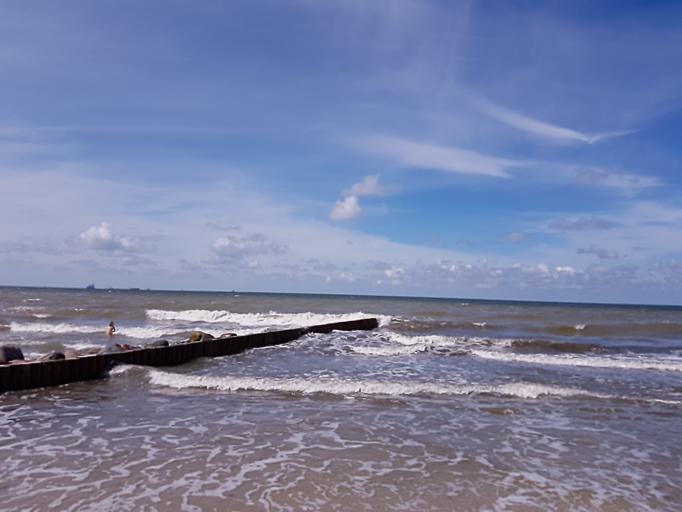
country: RU
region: Kaliningrad
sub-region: Zelenogradskiy Rayon
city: Zelenogradsk
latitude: 54.9600
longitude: 20.4682
